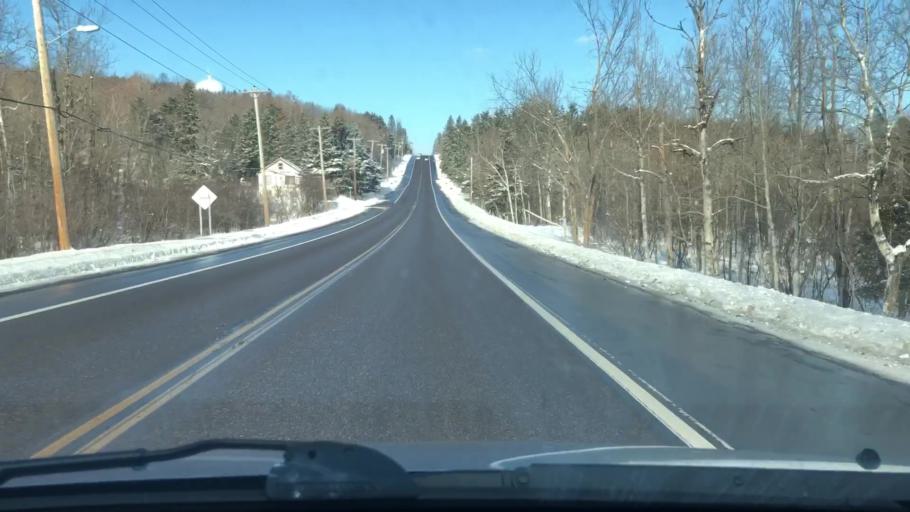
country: US
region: Minnesota
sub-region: Saint Louis County
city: Duluth
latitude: 46.8084
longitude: -92.1321
